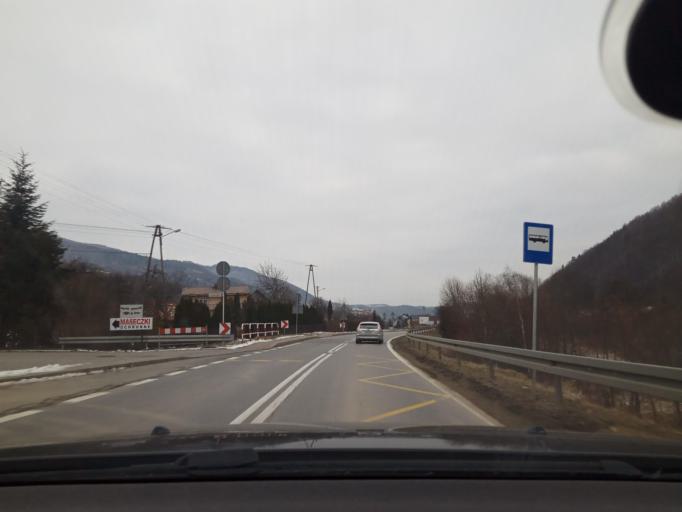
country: PL
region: Lesser Poland Voivodeship
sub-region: Powiat nowotarski
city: Kroscienko nad Dunajcem
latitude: 49.4797
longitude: 20.4149
